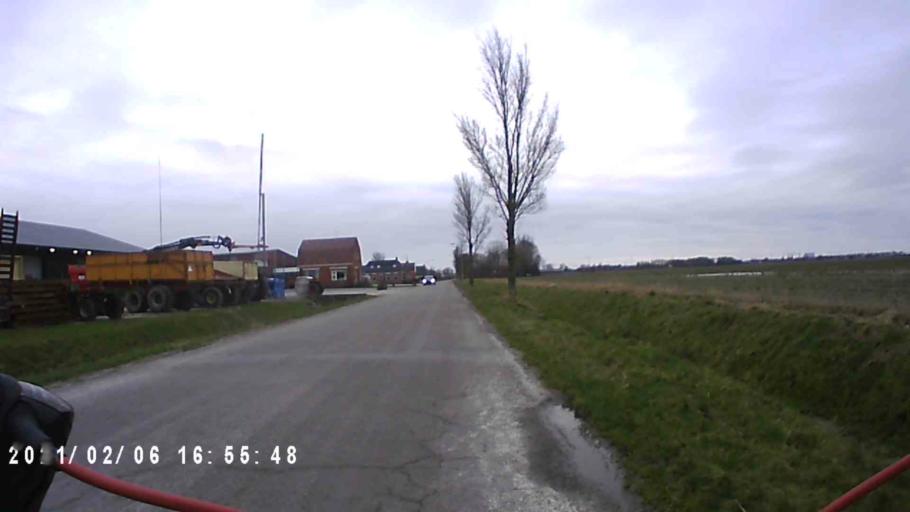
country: NL
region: Groningen
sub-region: Gemeente Appingedam
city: Appingedam
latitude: 53.4114
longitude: 6.7544
